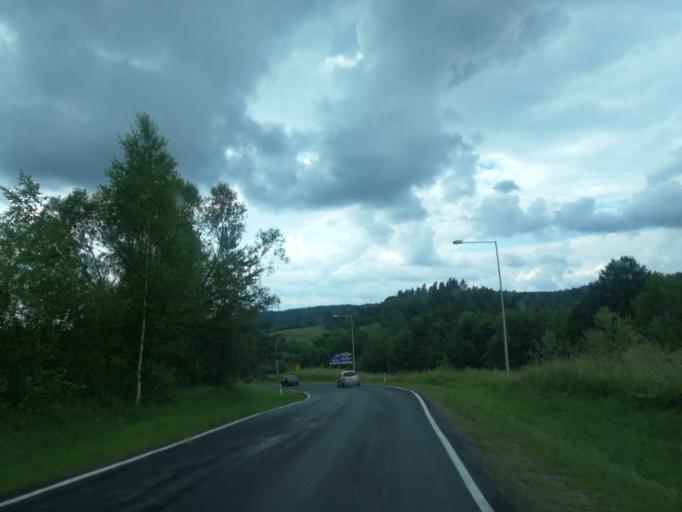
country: PL
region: Subcarpathian Voivodeship
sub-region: Powiat leski
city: Olszanica
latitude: 49.4410
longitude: 22.4531
